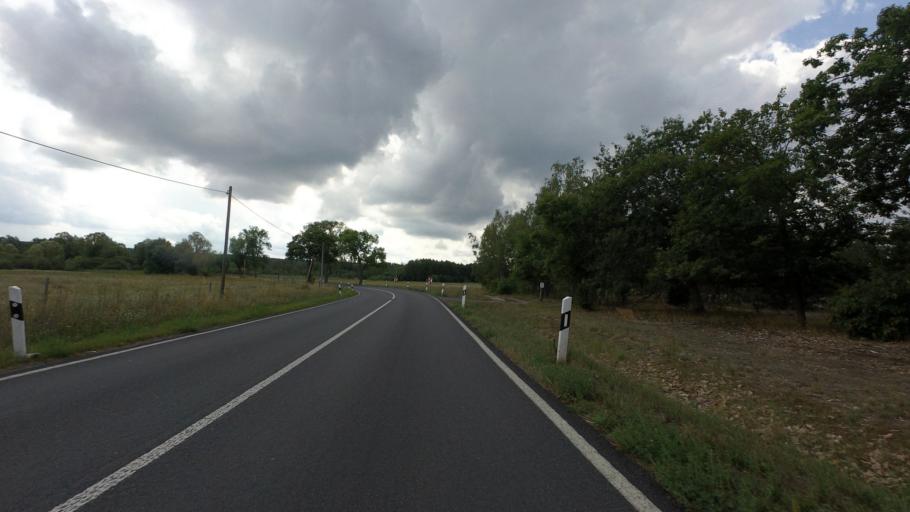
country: DE
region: Brandenburg
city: Teupitz
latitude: 52.1639
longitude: 13.5762
